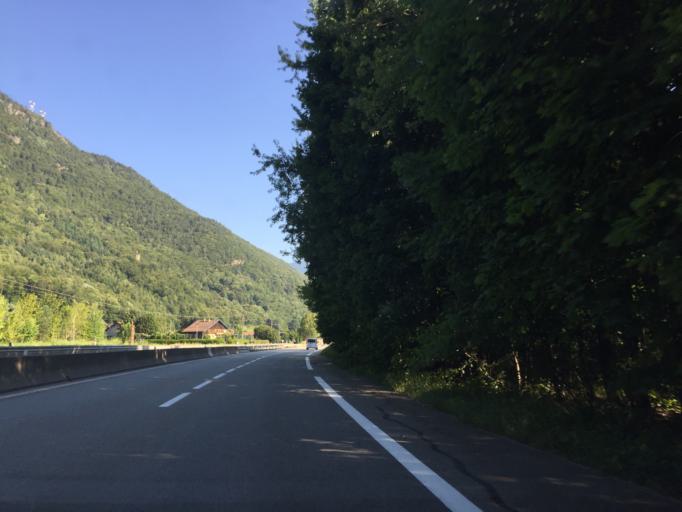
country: FR
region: Rhone-Alpes
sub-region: Departement de la Savoie
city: La Bathie
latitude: 45.5659
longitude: 6.4689
